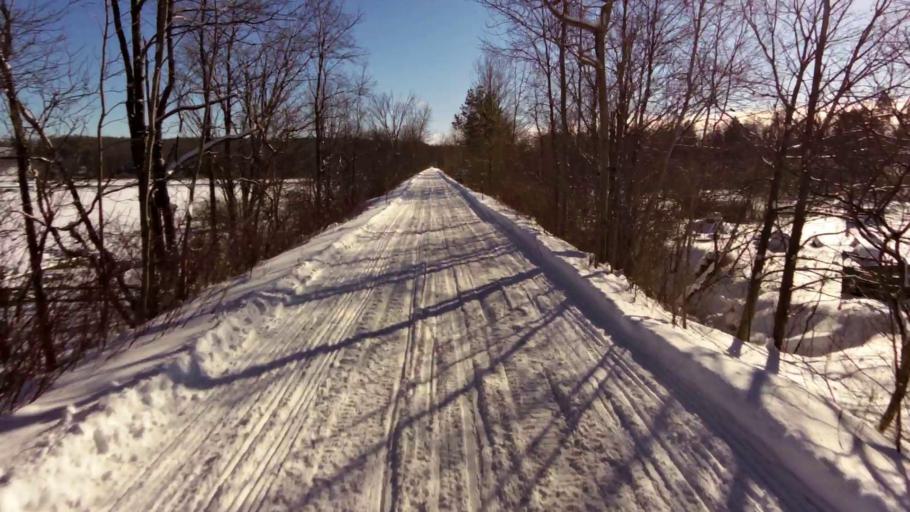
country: US
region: New York
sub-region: Chautauqua County
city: Mayville
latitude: 42.1619
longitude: -79.5853
